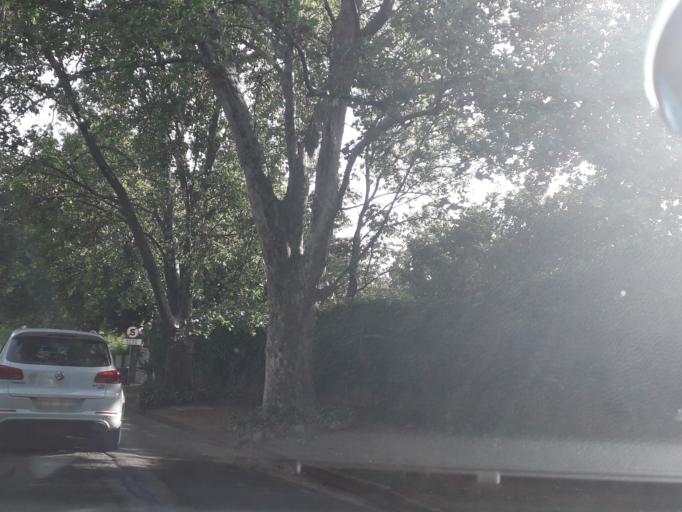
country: ZA
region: Gauteng
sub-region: City of Johannesburg Metropolitan Municipality
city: Johannesburg
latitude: -26.1579
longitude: 28.0225
